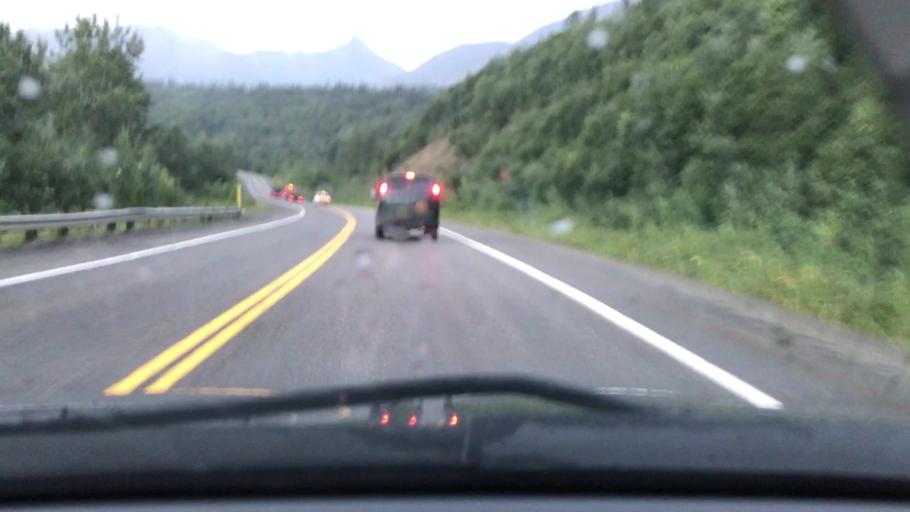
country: US
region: Alaska
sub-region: Matanuska-Susitna Borough
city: Y
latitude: 63.0459
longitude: -149.5762
